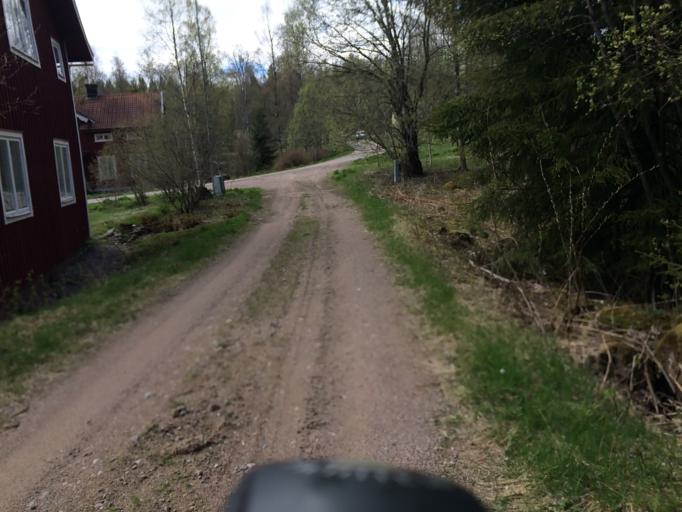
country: SE
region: OErebro
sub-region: Hallefors Kommun
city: Haellefors
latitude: 60.0433
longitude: 14.5145
